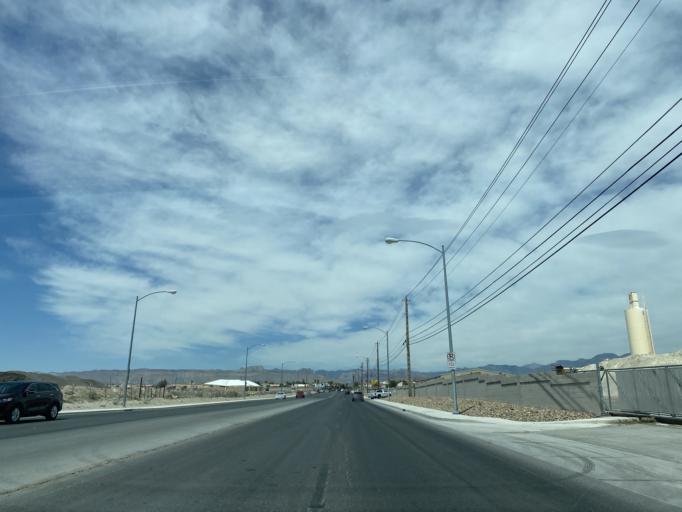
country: US
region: Nevada
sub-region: Clark County
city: Spring Valley
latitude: 36.1256
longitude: -115.2546
